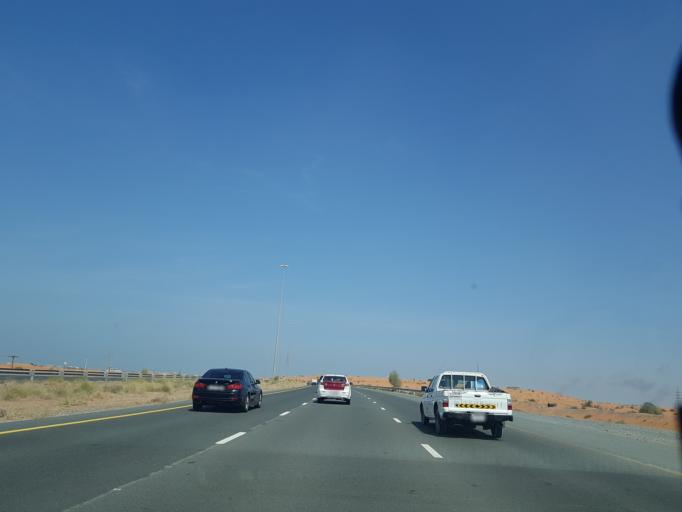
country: AE
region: Ra's al Khaymah
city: Ras al-Khaimah
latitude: 25.6769
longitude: 55.8834
